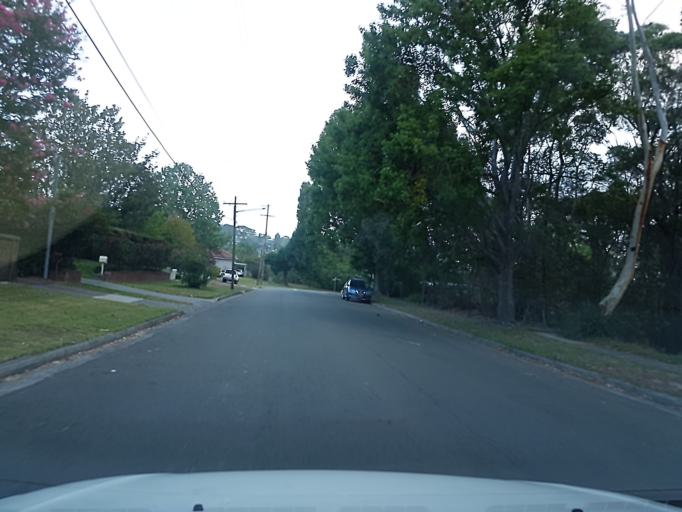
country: AU
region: New South Wales
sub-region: Warringah
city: Davidson
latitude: -33.7472
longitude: 151.2268
